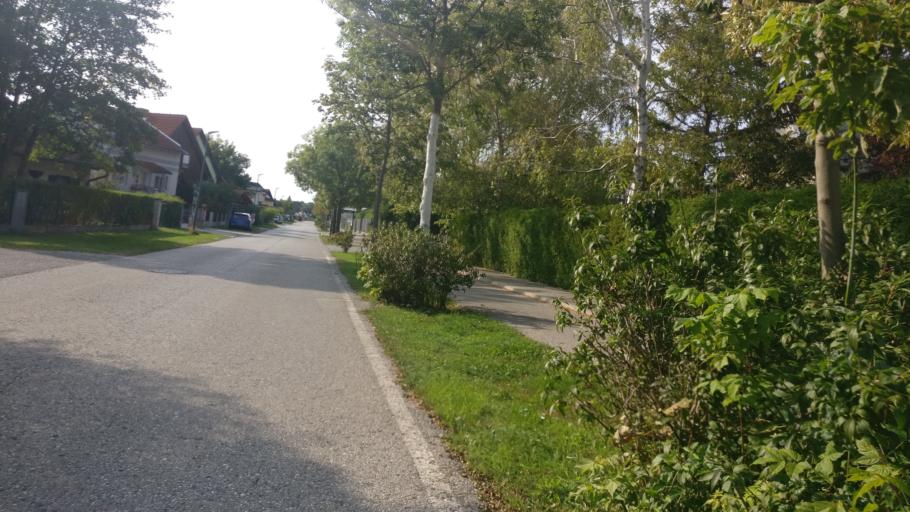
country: AT
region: Lower Austria
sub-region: Politischer Bezirk Baden
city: Ebreichsdorf
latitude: 47.9722
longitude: 16.4081
